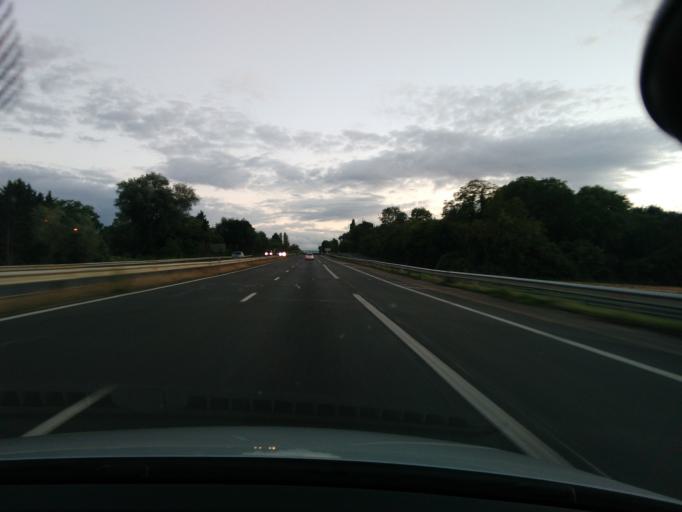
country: FR
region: Ile-de-France
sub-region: Departement de Seine-et-Marne
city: Nanteuil-les-Meaux
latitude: 48.9330
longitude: 2.8800
